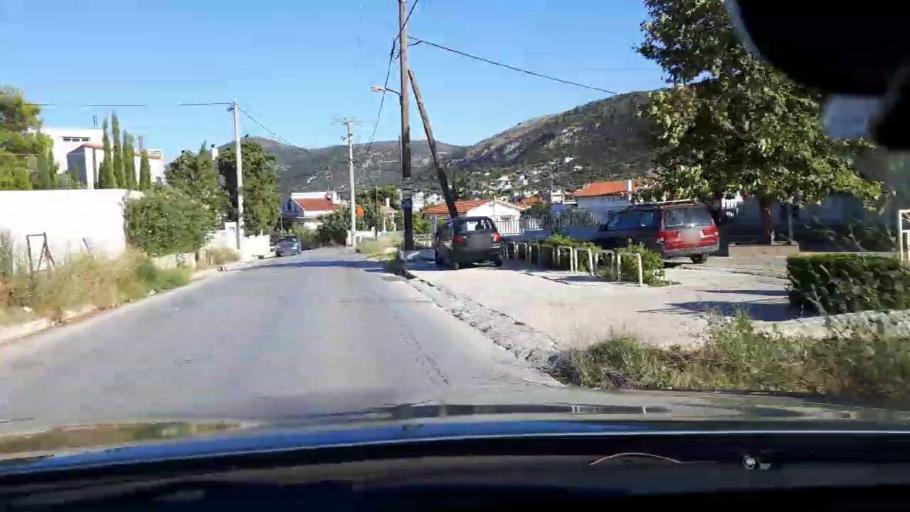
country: GR
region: Attica
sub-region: Nomarchia Anatolikis Attikis
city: Limin Mesoyaias
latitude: 37.8712
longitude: 24.0141
